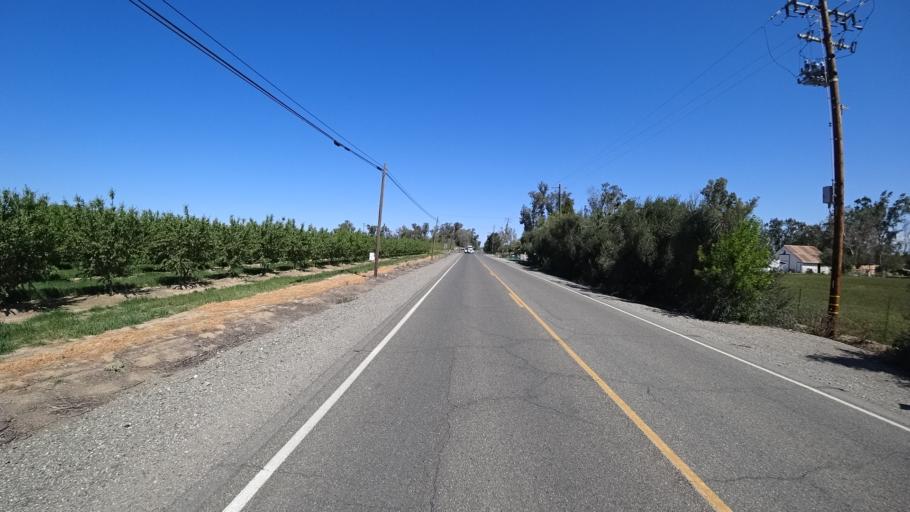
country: US
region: California
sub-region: Glenn County
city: Orland
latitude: 39.7098
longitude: -122.1971
